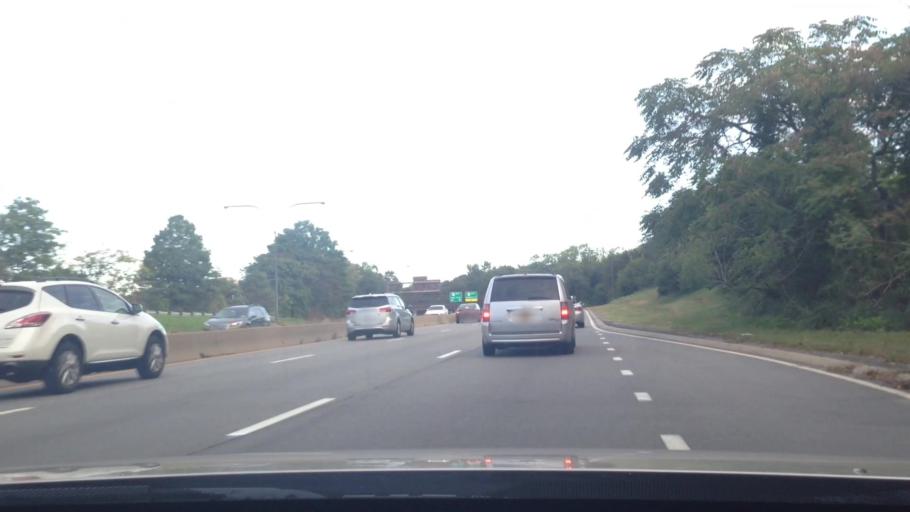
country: US
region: New York
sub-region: Nassau County
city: Carle Place
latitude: 40.7439
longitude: -73.6116
